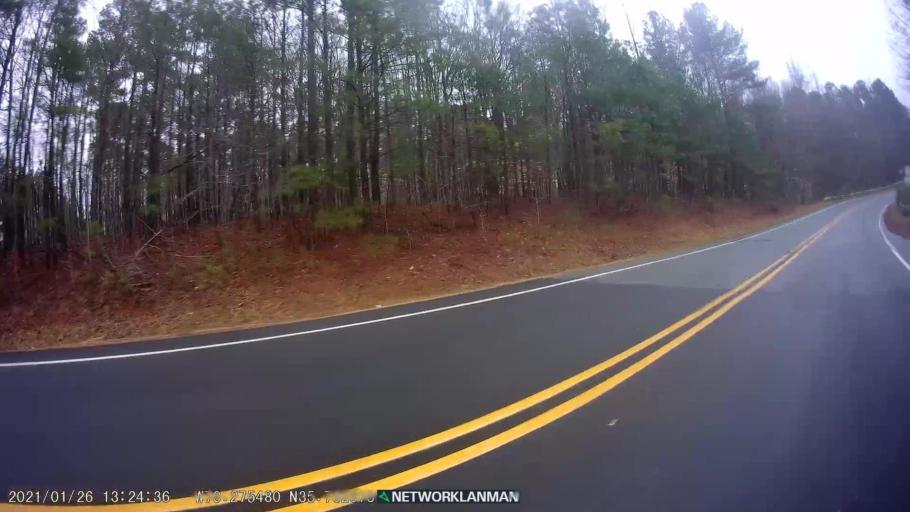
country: US
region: North Carolina
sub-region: Chatham County
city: Pittsboro
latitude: 35.7325
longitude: -79.2755
